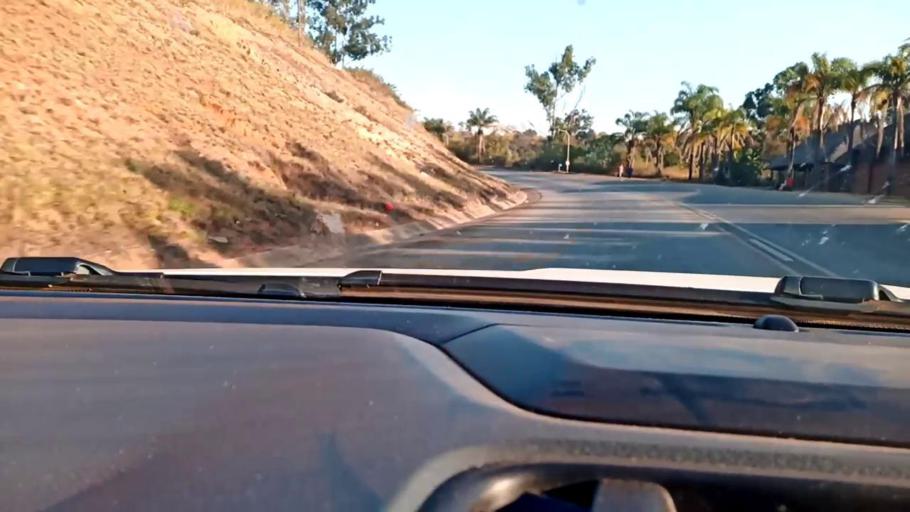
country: ZA
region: Limpopo
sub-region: Mopani District Municipality
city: Duiwelskloof
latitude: -23.6897
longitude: 30.1468
